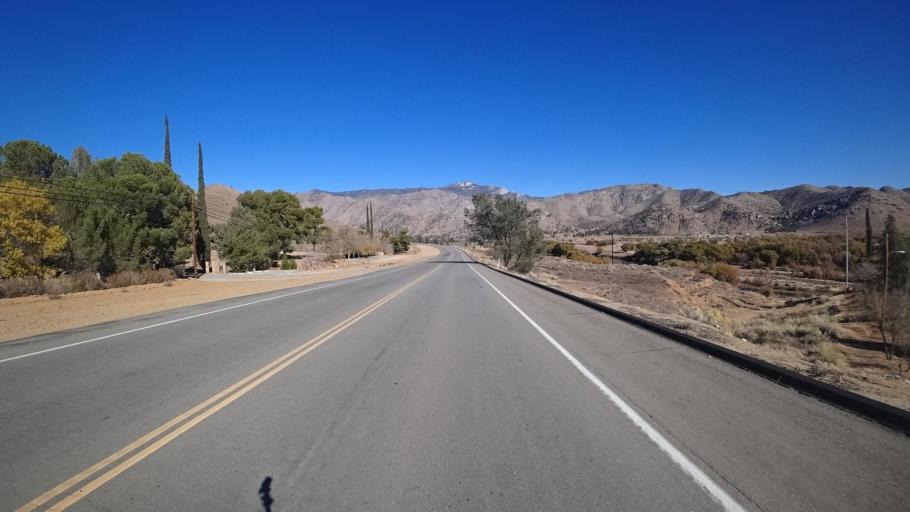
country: US
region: California
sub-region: Kern County
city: Wofford Heights
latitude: 35.7205
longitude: -118.4361
